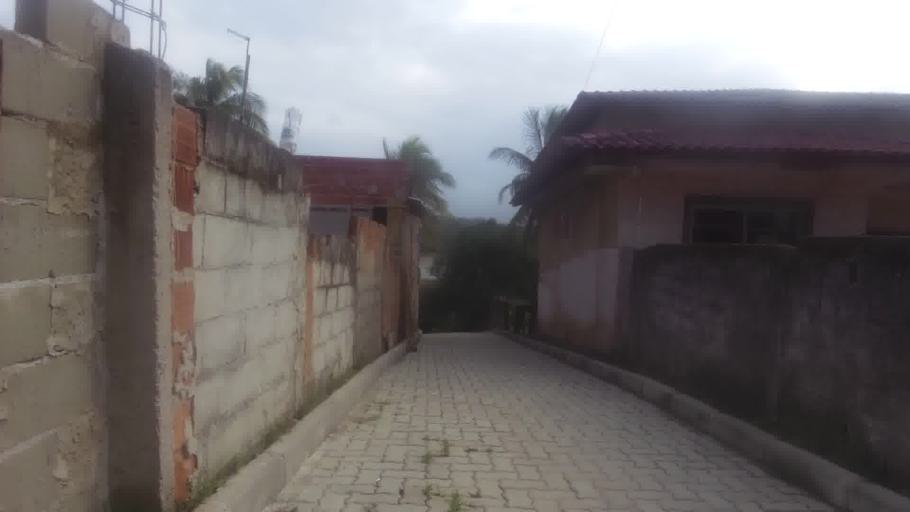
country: BR
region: Espirito Santo
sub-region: Guarapari
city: Guarapari
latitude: -20.7650
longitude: -40.5772
